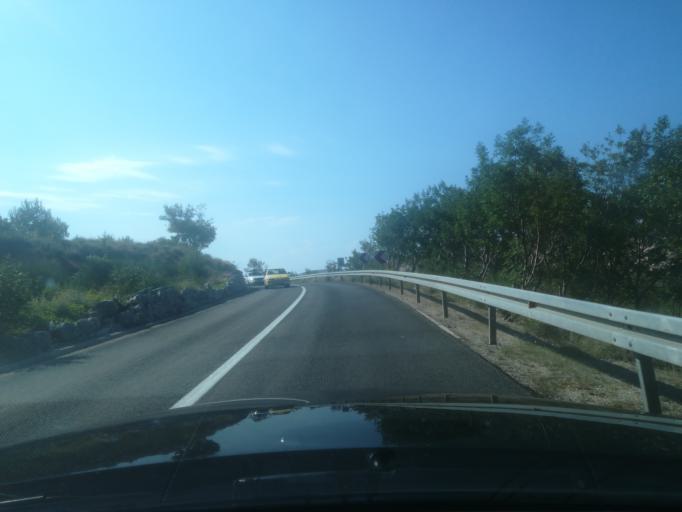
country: HR
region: Primorsko-Goranska
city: Banjol
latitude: 44.7132
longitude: 14.8281
